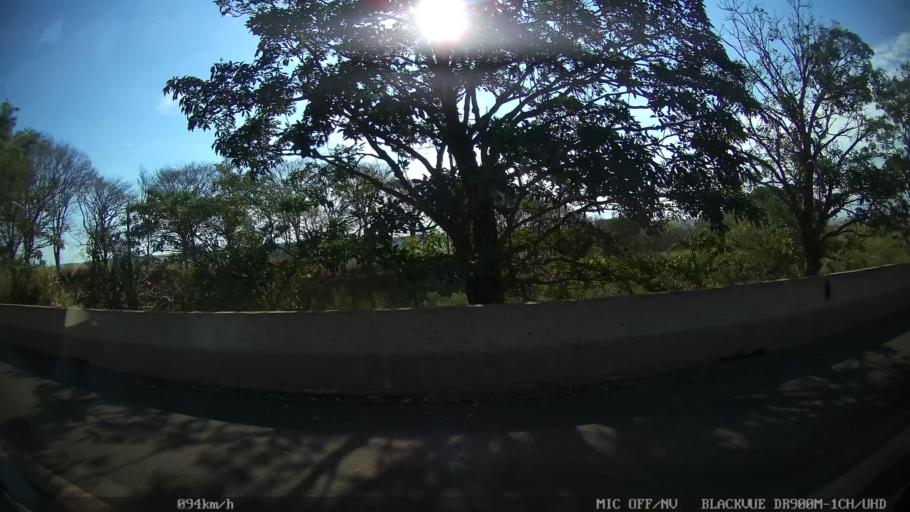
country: BR
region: Sao Paulo
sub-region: Iracemapolis
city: Iracemapolis
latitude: -22.6743
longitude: -47.5597
